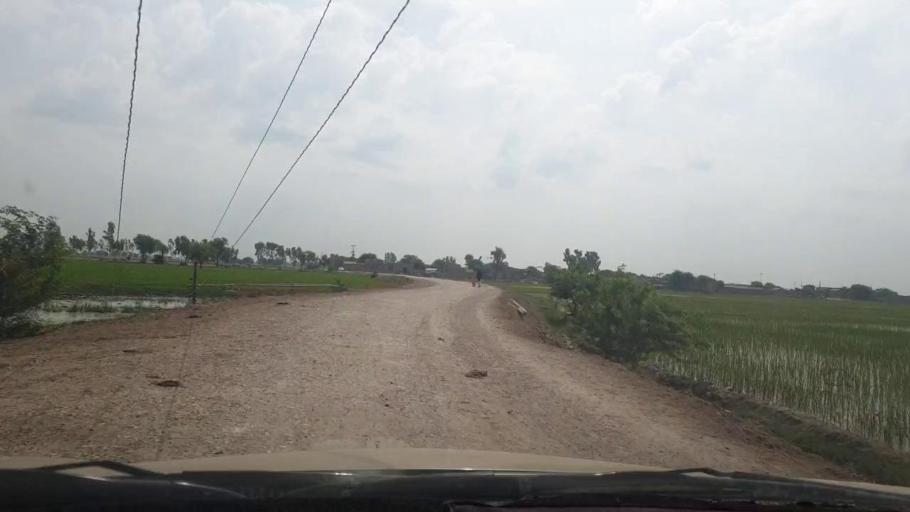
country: PK
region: Sindh
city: Larkana
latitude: 27.6775
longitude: 68.1895
